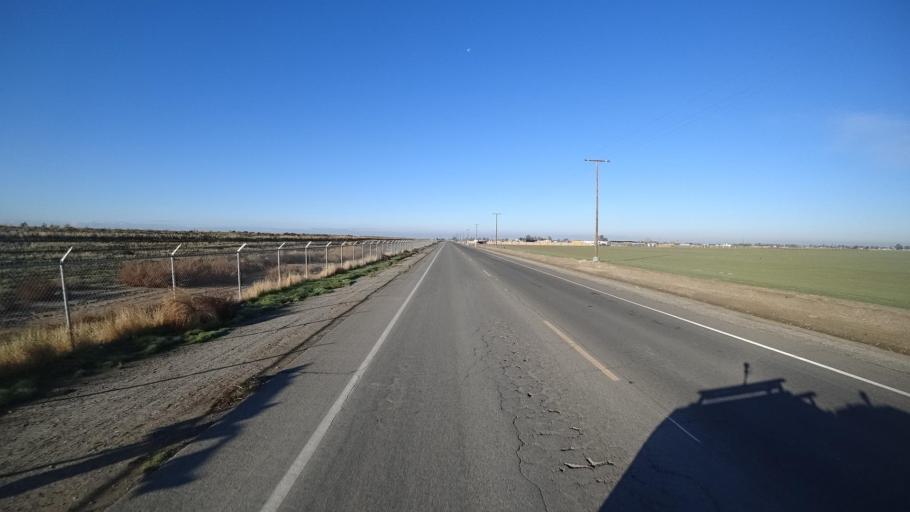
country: US
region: California
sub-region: Kern County
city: Delano
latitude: 35.7759
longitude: -119.2871
